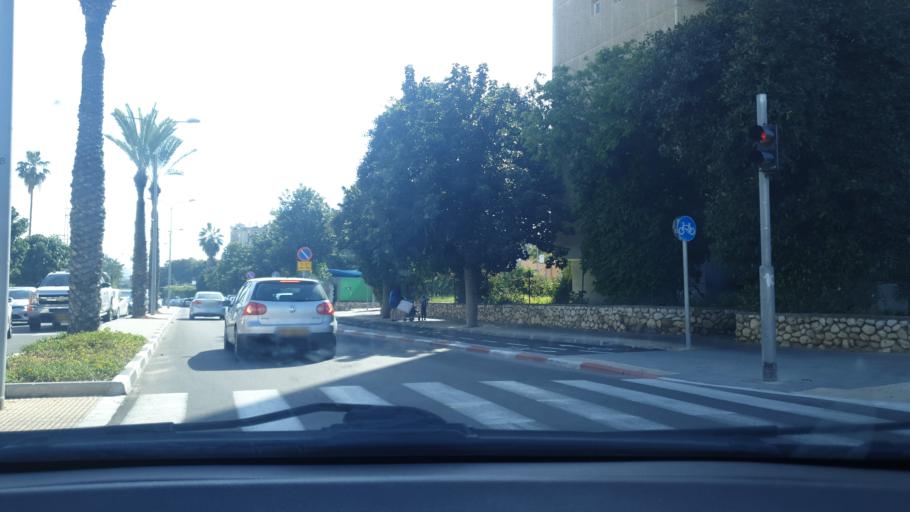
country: IL
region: Tel Aviv
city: Azor
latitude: 32.0458
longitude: 34.8046
